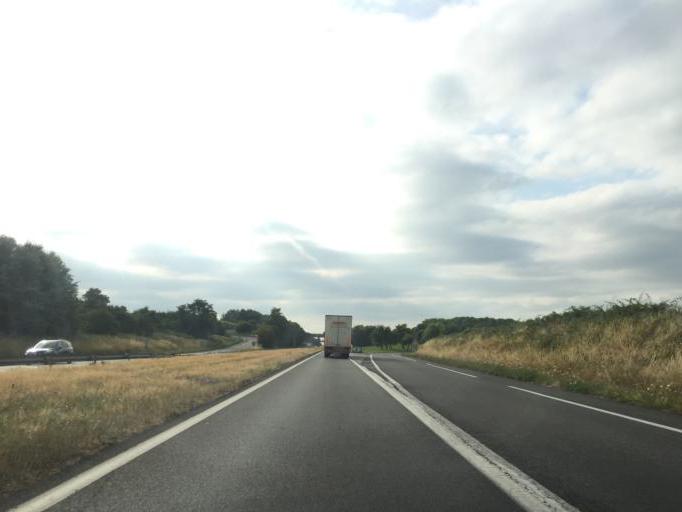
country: FR
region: Auvergne
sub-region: Departement de l'Allier
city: Dompierre-sur-Besbre
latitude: 46.5281
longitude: 3.7228
